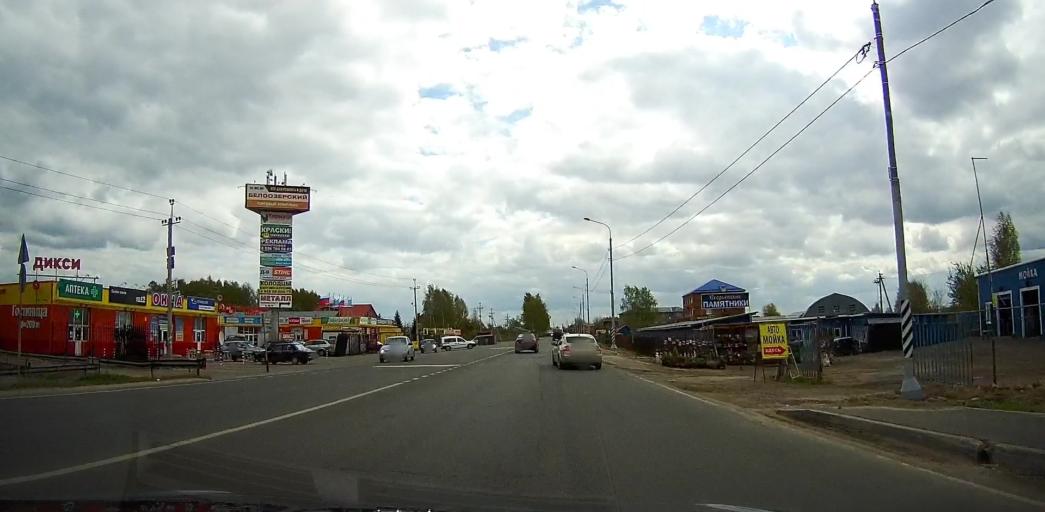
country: RU
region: Moskovskaya
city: Beloozerskiy
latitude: 55.4517
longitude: 38.4376
